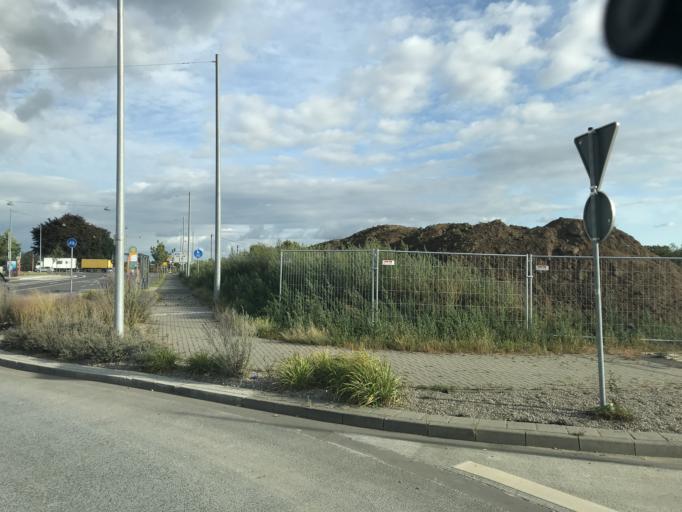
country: DE
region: Rheinland-Pfalz
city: Mainz
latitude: 50.0264
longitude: 8.2891
